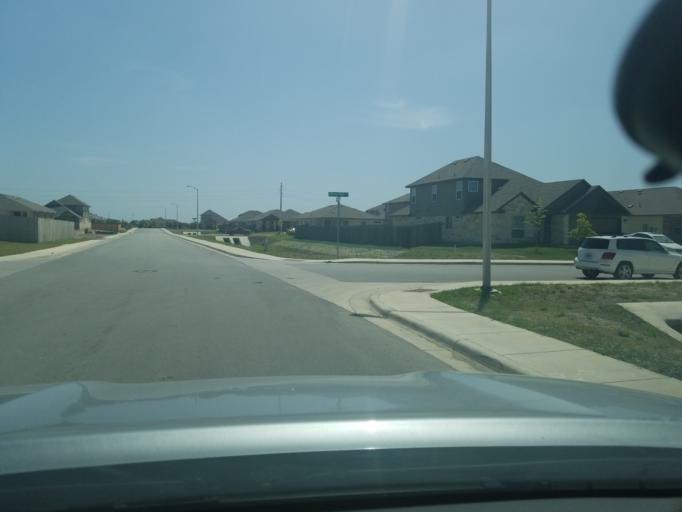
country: US
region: Texas
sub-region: Guadalupe County
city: Lake Dunlap
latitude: 29.6731
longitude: -98.0355
